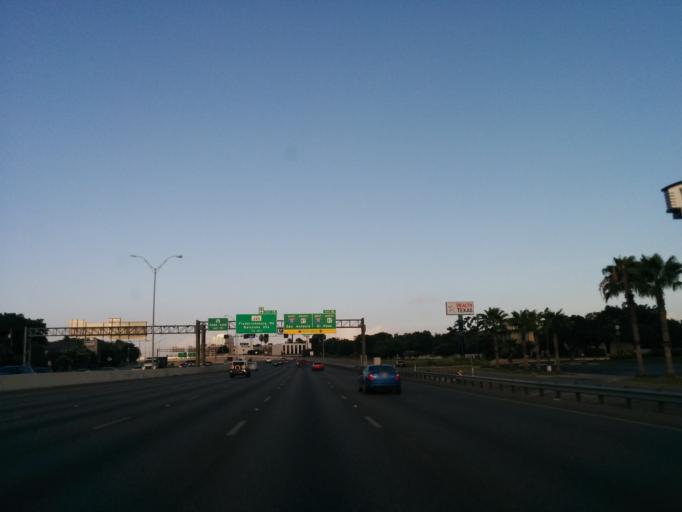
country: US
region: Texas
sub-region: Bexar County
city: Balcones Heights
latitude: 29.5103
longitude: -98.5392
